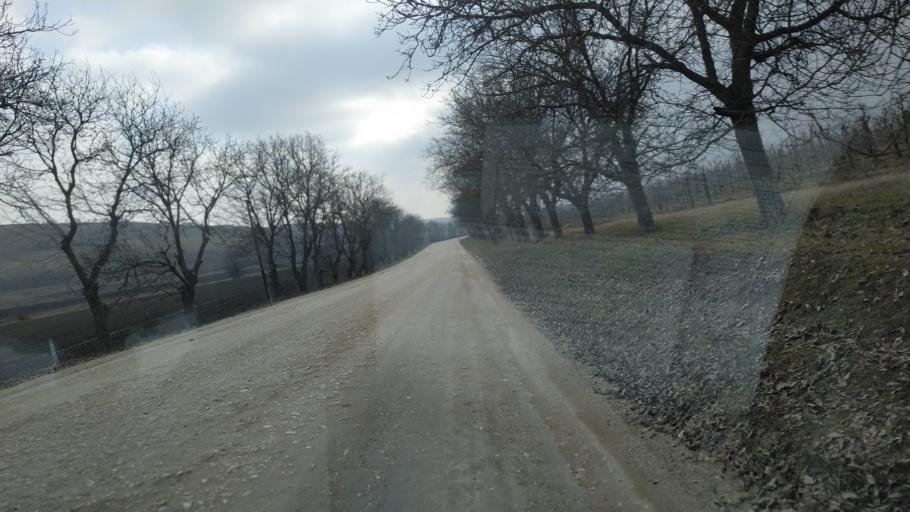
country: MD
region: Hincesti
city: Dancu
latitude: 46.9142
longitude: 28.3292
